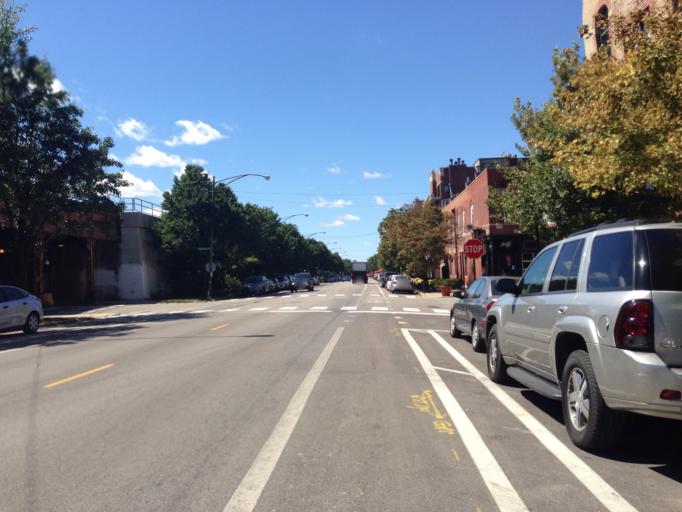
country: US
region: Illinois
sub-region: Cook County
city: Chicago
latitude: 41.8900
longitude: -87.6541
